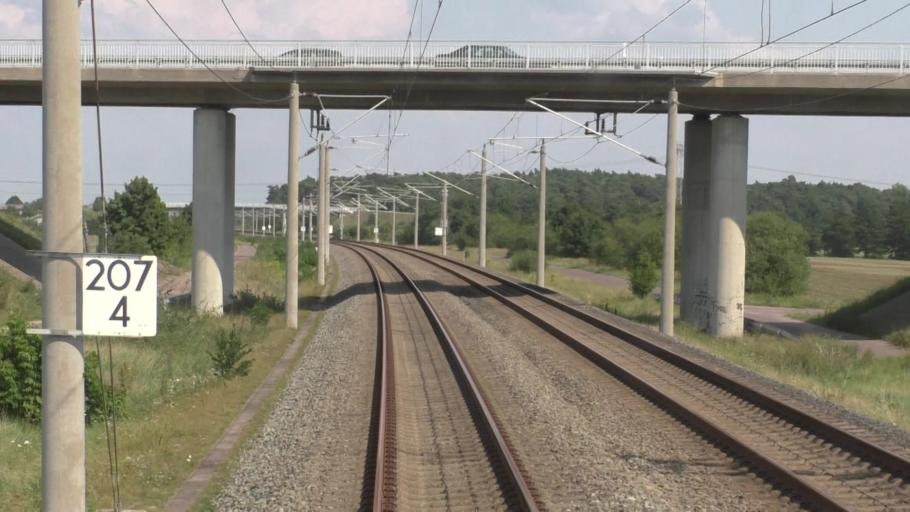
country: DE
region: Saxony-Anhalt
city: Stendal
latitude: 52.5724
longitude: 11.8300
